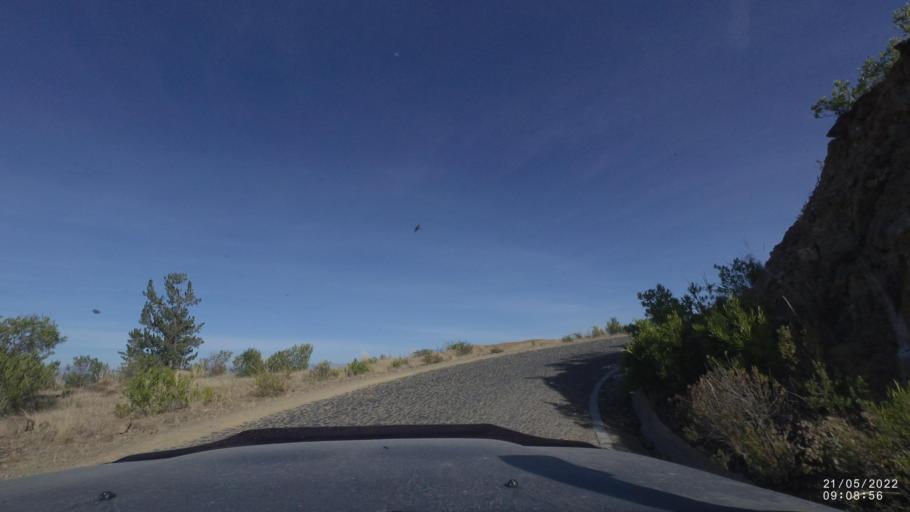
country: BO
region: Cochabamba
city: Cochabamba
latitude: -17.3755
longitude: -66.0228
